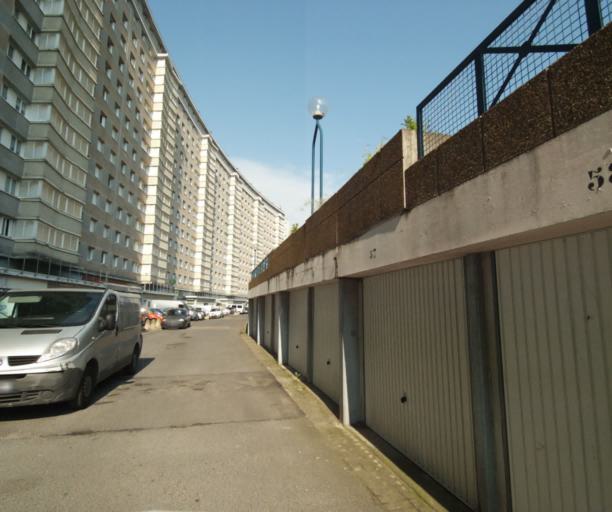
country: FR
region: Ile-de-France
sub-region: Departement du Val-d'Oise
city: Sannois
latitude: 48.9615
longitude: 2.2477
